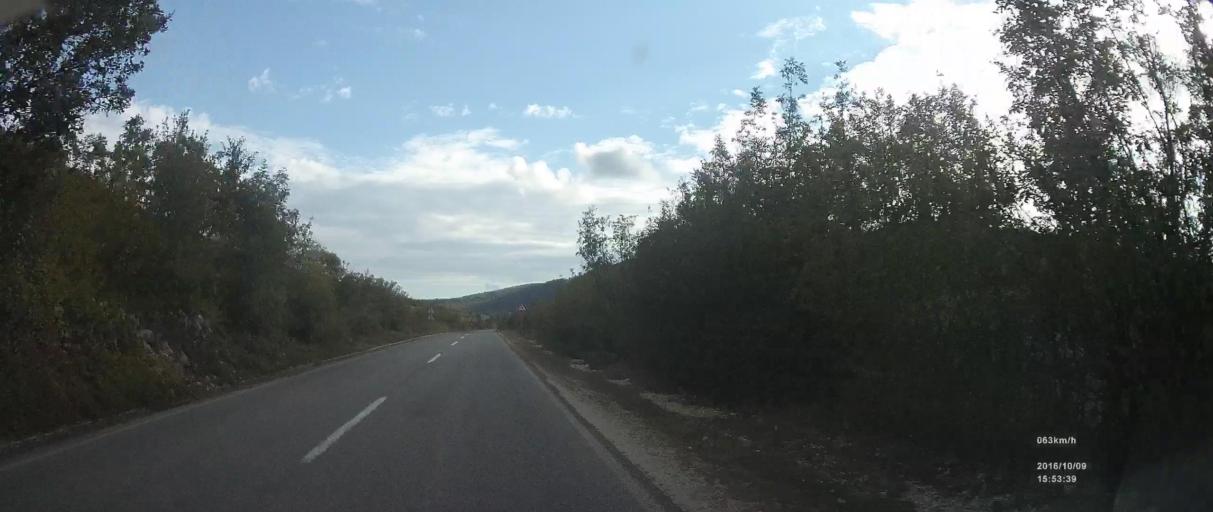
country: HR
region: Splitsko-Dalmatinska
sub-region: Grad Trogir
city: Trogir
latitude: 43.6033
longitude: 16.2247
